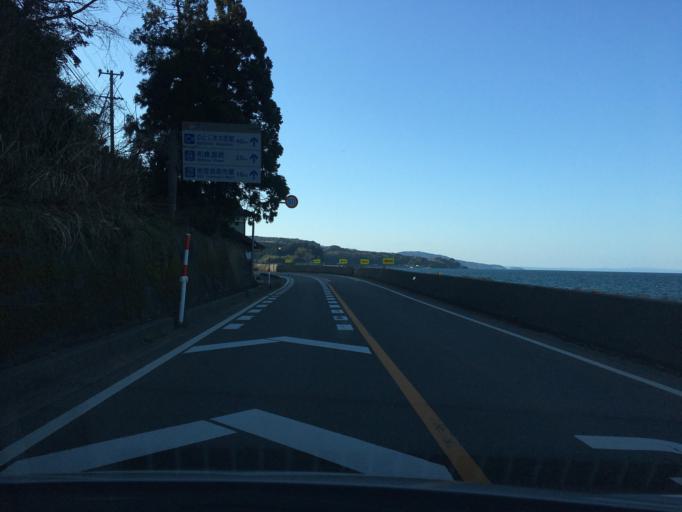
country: JP
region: Ishikawa
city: Nanao
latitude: 36.9689
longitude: 137.0560
